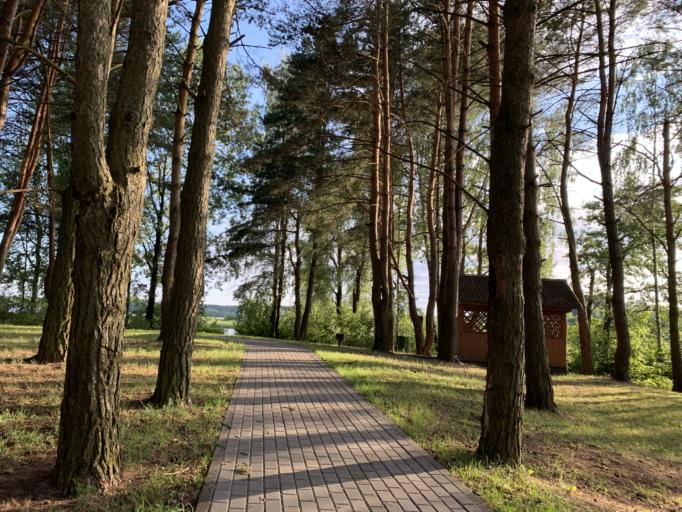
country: BY
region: Minsk
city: Khatsyezhyna
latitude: 53.9731
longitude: 27.3421
